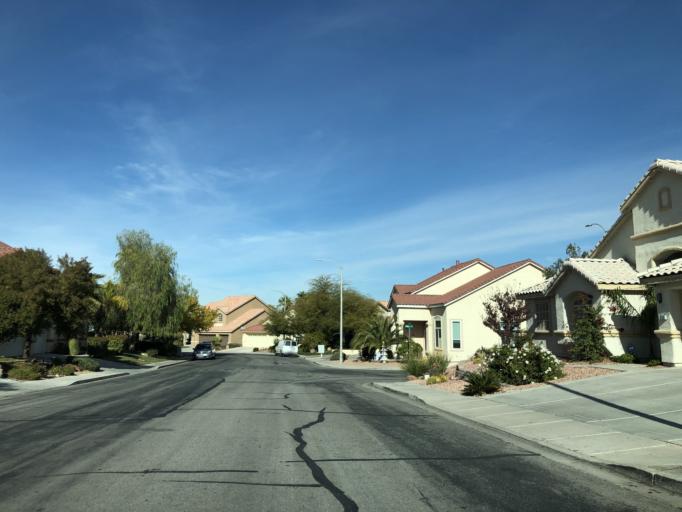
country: US
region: Nevada
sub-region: Clark County
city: Whitney
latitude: 36.0139
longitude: -115.0800
